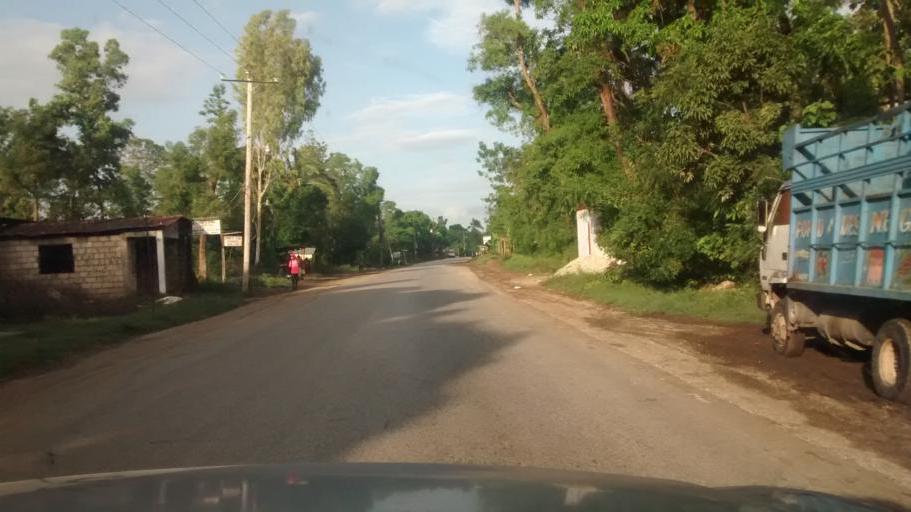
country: HT
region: Nippes
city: Miragoane
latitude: 18.4236
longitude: -73.0019
